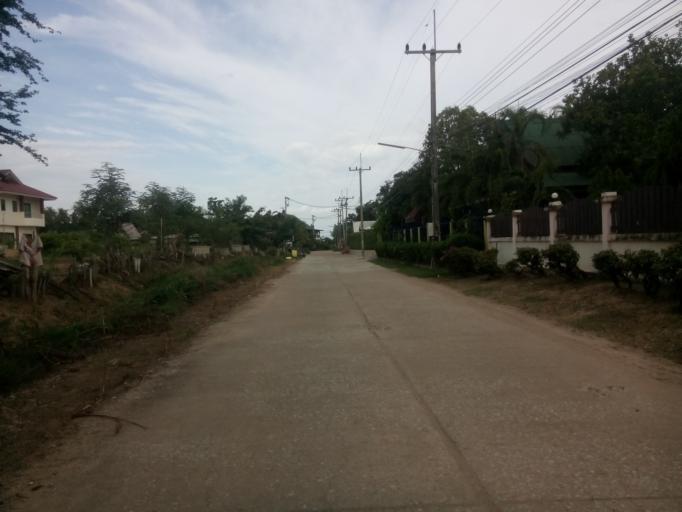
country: TH
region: Sukhothai
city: Ban Na
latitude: 17.0133
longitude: 99.7148
